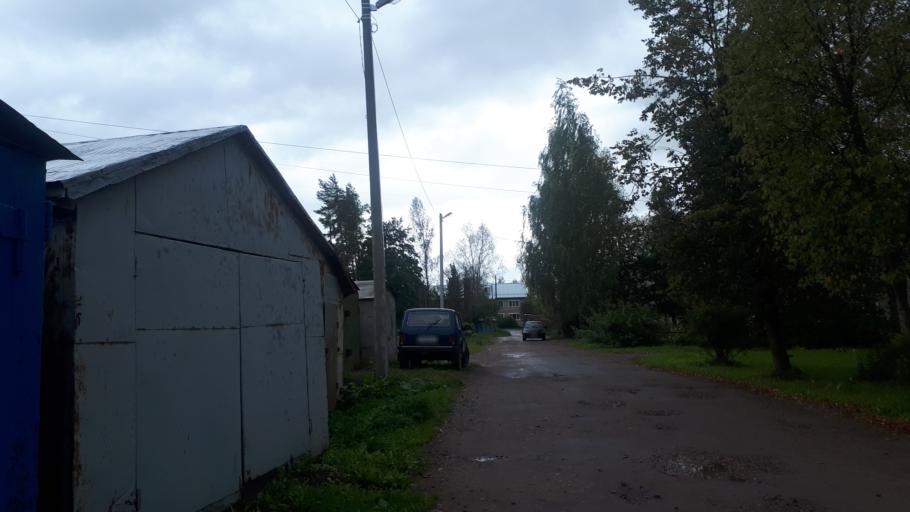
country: RU
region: Jaroslavl
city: Konstantinovskiy
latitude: 57.8286
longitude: 39.5871
